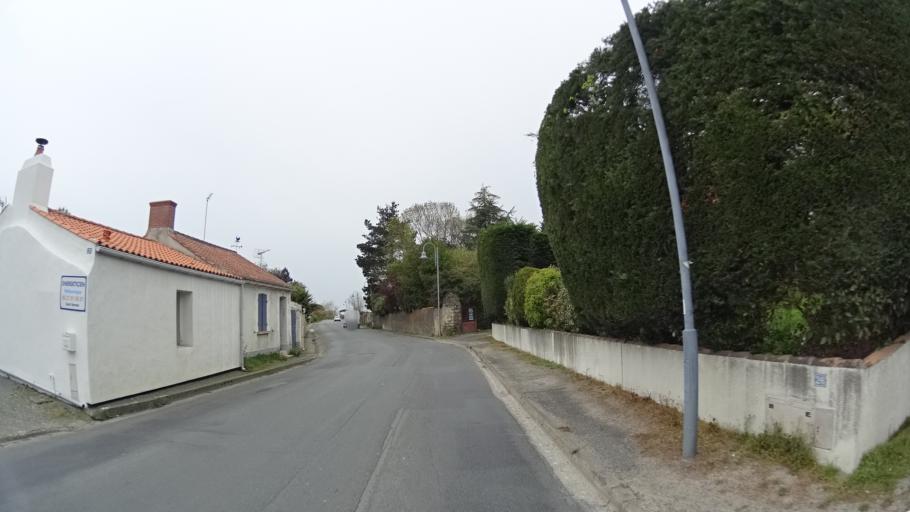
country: FR
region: Pays de la Loire
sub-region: Departement de la Vendee
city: Saint-Gervais
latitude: 46.9026
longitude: -2.0035
